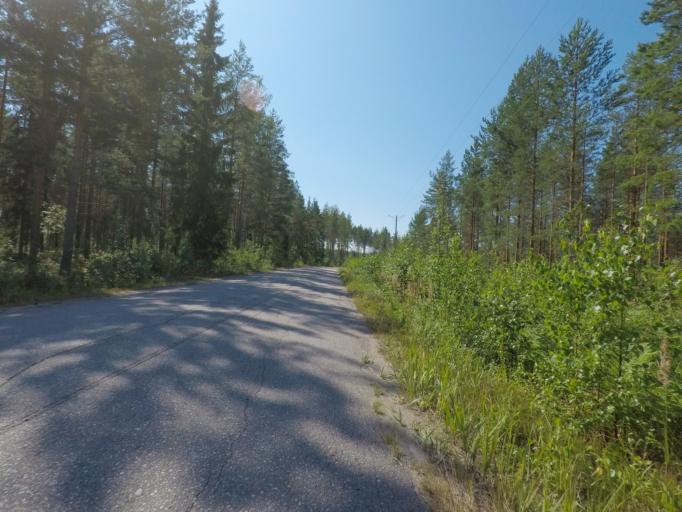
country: FI
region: Southern Savonia
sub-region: Mikkeli
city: Puumala
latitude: 61.4252
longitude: 28.1571
